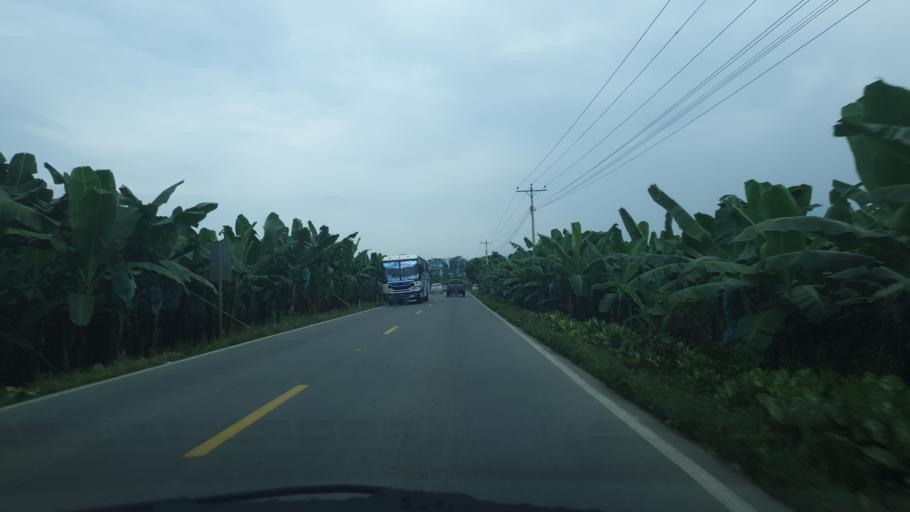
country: EC
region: El Oro
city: Pasaje
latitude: -3.3540
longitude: -79.8203
